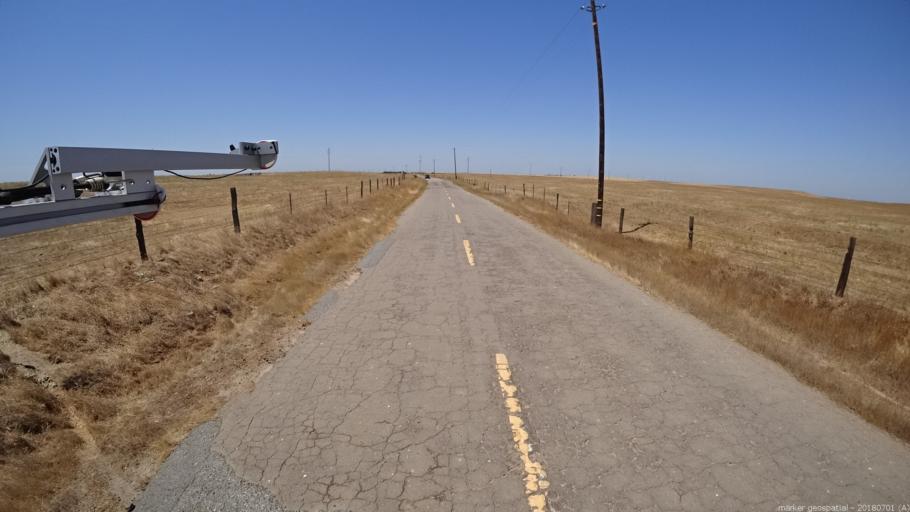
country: US
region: California
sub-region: Madera County
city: Madera Acres
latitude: 37.0997
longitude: -120.0028
